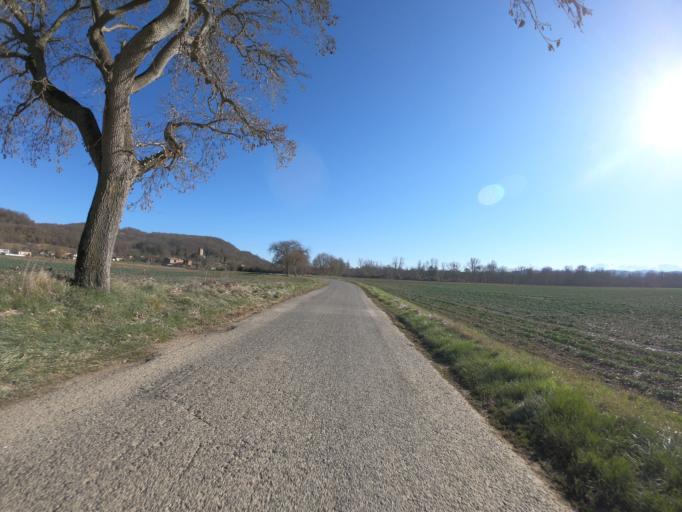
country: FR
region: Midi-Pyrenees
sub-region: Departement de l'Ariege
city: La Tour-du-Crieu
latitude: 43.0967
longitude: 1.7547
